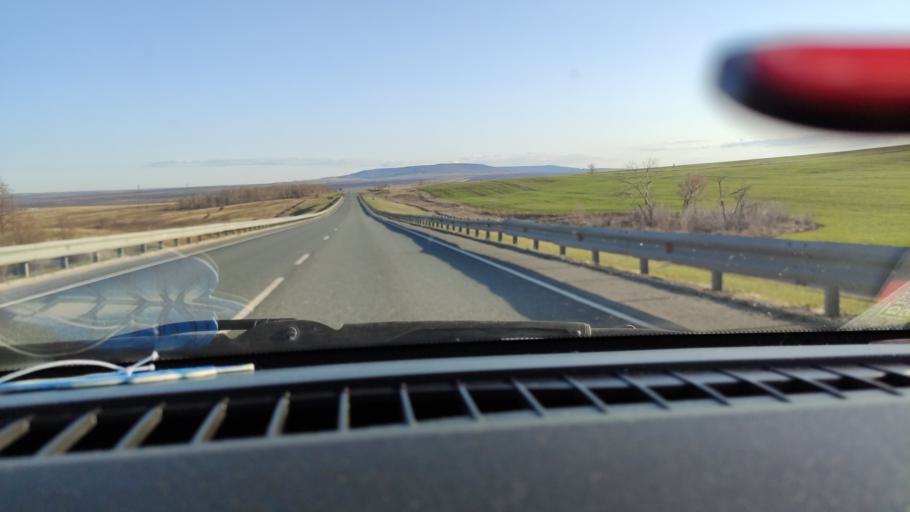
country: RU
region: Saratov
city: Alekseyevka
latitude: 52.2274
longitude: 47.9020
